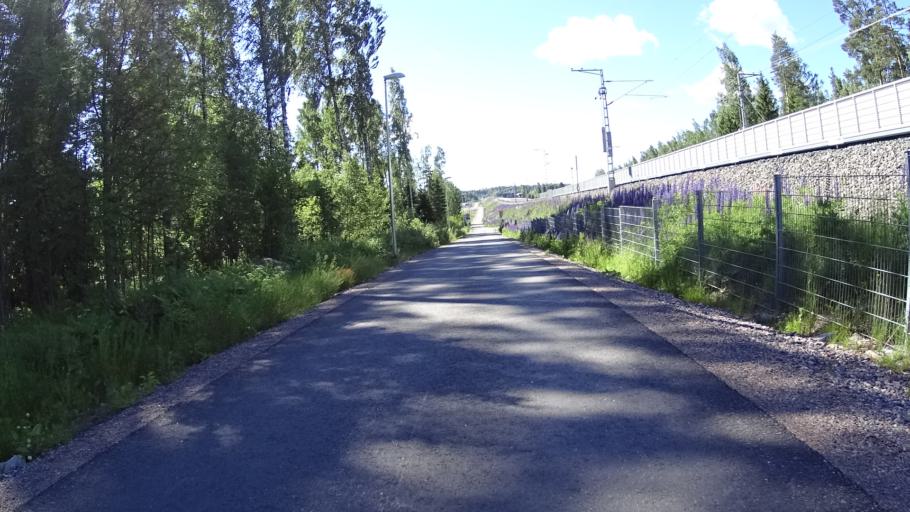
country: FI
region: Uusimaa
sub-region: Helsinki
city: Kilo
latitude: 60.2994
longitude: 24.8427
